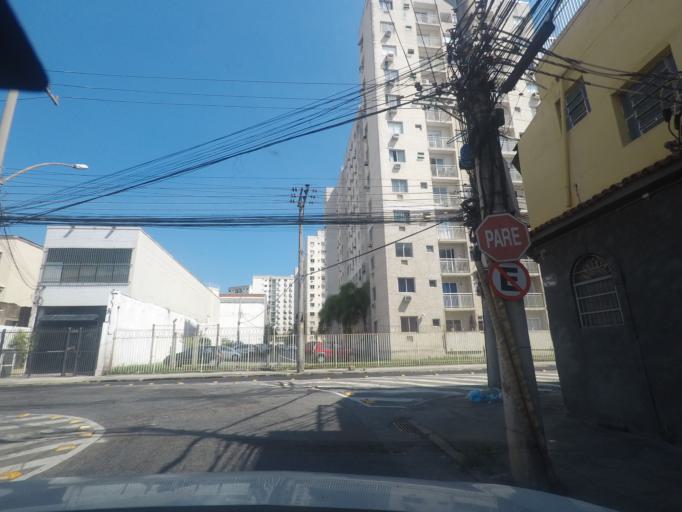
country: BR
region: Rio de Janeiro
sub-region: Rio De Janeiro
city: Rio de Janeiro
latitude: -22.8915
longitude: -43.2206
